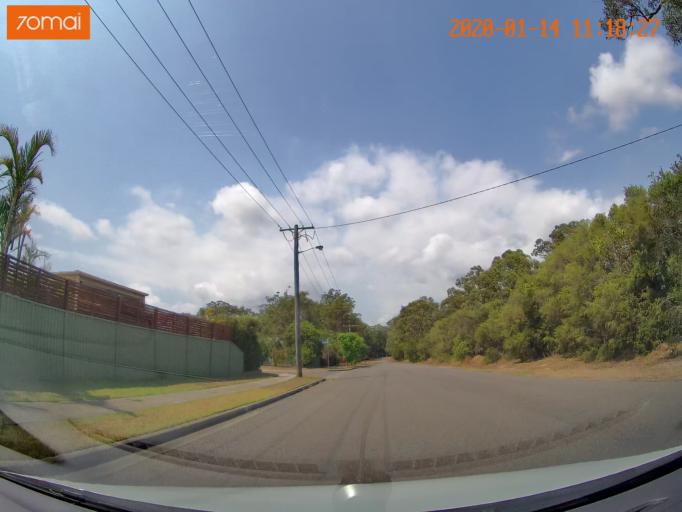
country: AU
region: New South Wales
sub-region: Lake Macquarie Shire
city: Cooranbong
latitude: -33.0973
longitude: 151.4605
